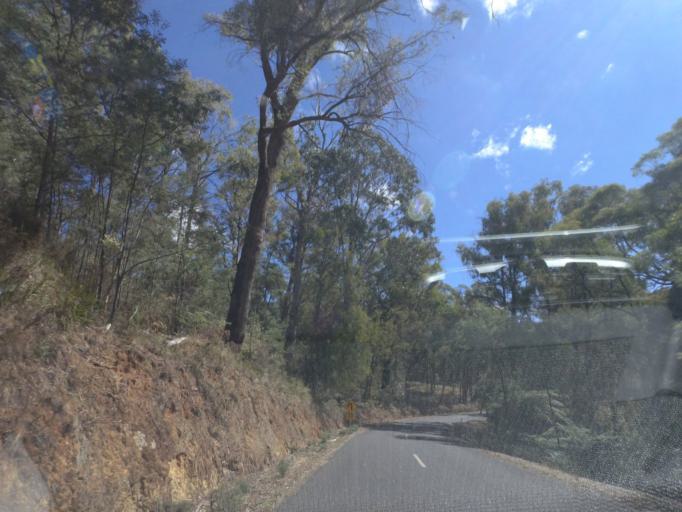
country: AU
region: Victoria
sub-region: Murrindindi
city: Alexandra
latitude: -37.3291
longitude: 145.9407
